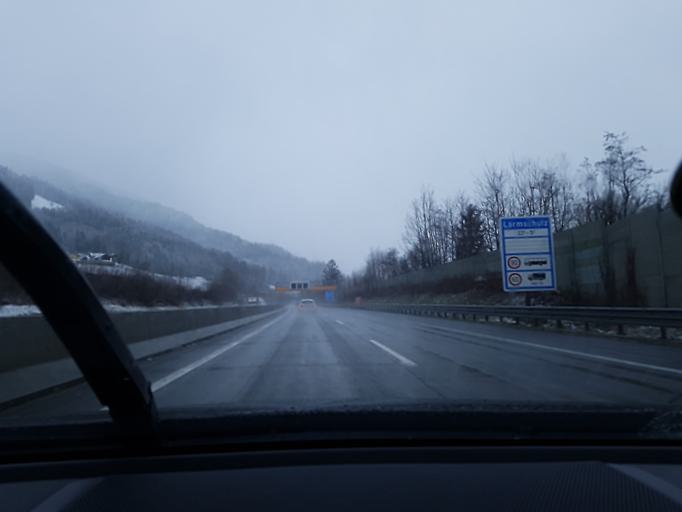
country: AT
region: Salzburg
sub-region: Politischer Bezirk Hallein
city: Kuchl
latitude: 47.6093
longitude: 13.1449
